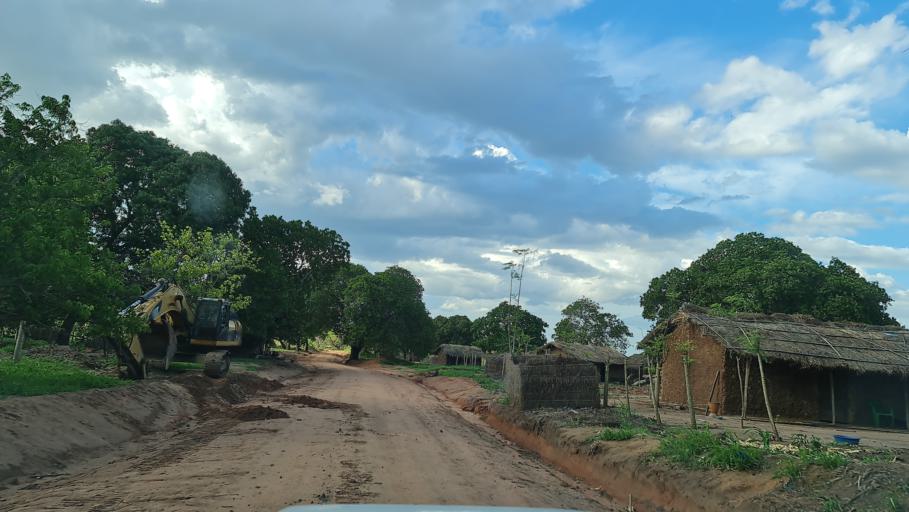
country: MZ
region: Cabo Delgado
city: Pemba
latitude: -13.5539
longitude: 40.1036
